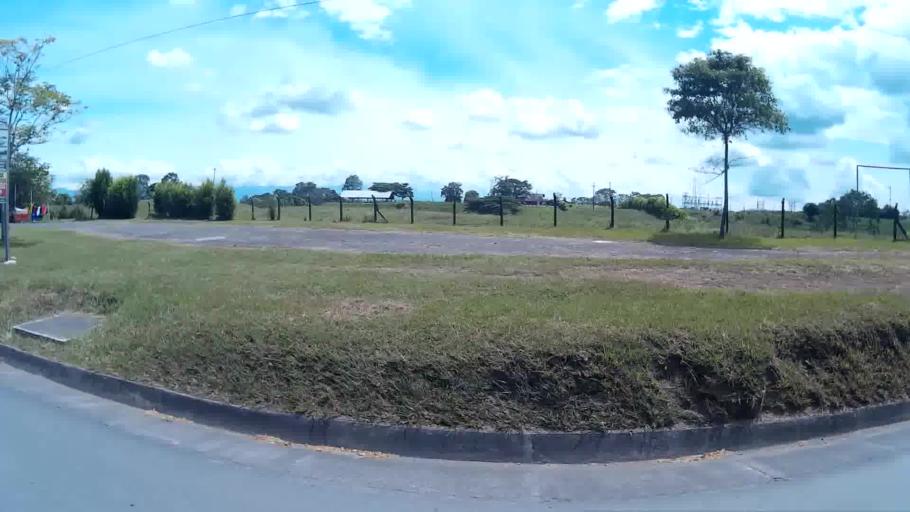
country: CO
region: Risaralda
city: Pereira
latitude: 4.8109
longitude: -75.8096
